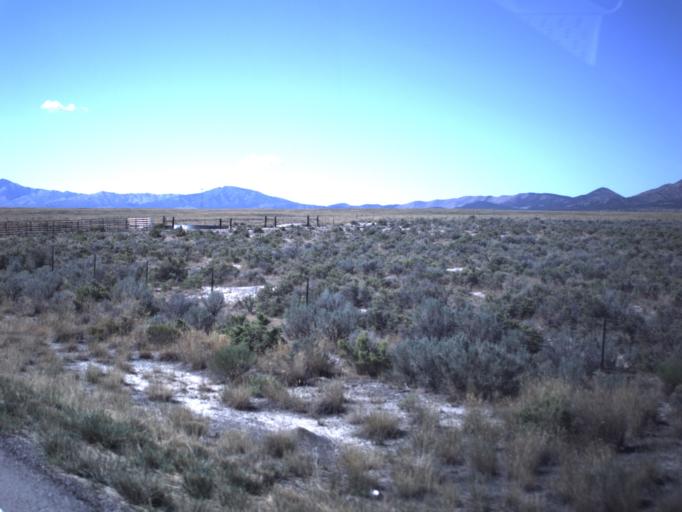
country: US
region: Utah
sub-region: Tooele County
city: Tooele
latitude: 40.2171
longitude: -112.4060
